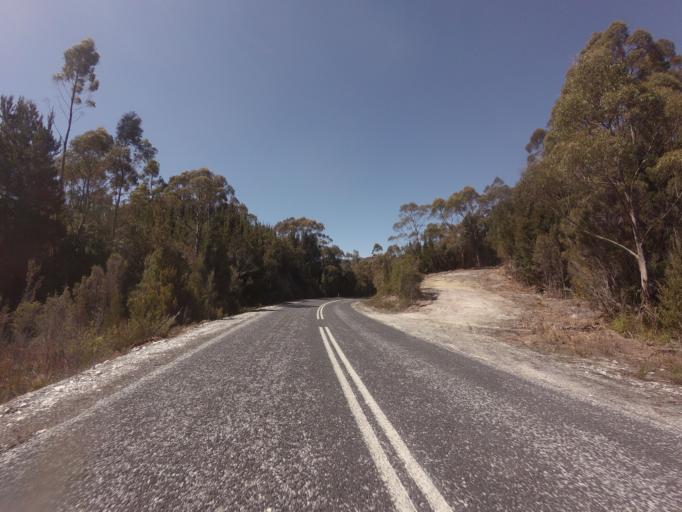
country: AU
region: Tasmania
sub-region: Huon Valley
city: Geeveston
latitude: -42.8211
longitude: 146.1168
